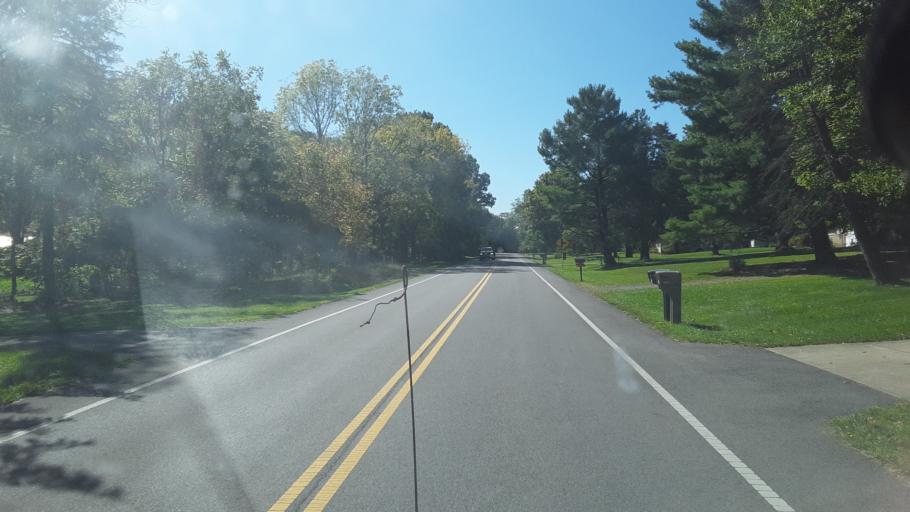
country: US
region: Ohio
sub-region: Delaware County
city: Sunbury
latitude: 40.2033
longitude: -82.8953
